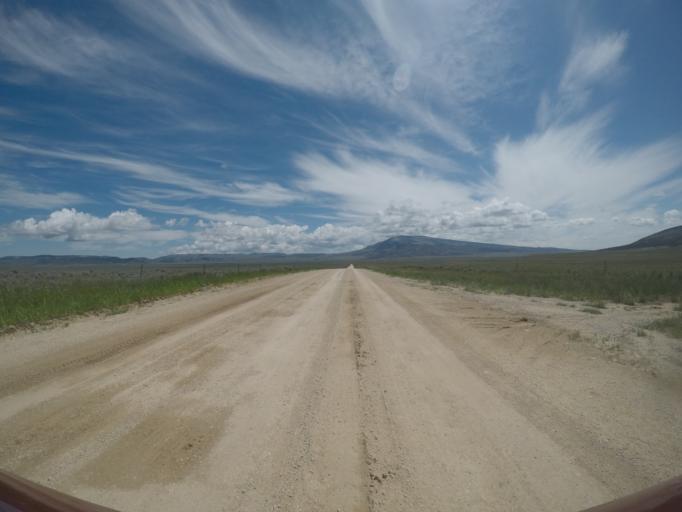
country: US
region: Wyoming
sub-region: Park County
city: Powell
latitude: 45.2051
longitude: -108.7546
